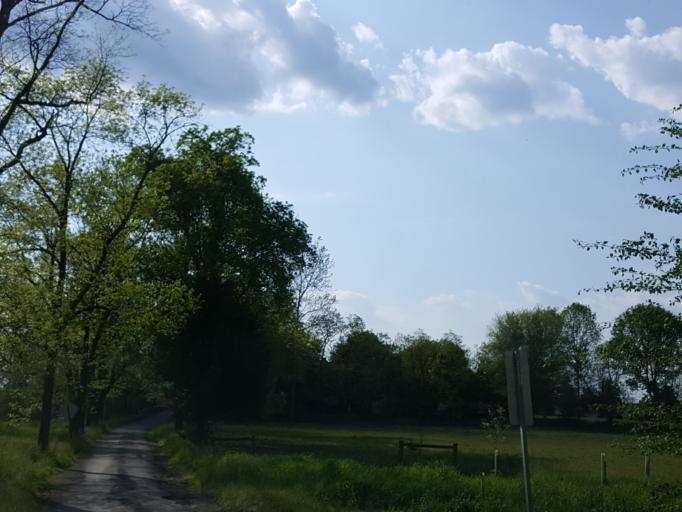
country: US
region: Pennsylvania
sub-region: Lancaster County
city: Elizabethtown
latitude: 40.1953
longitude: -76.5679
